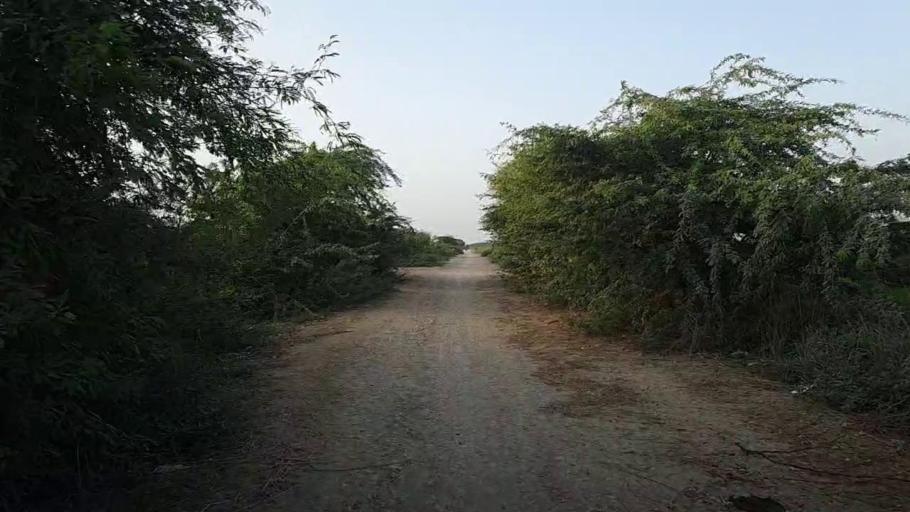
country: PK
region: Sindh
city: Kario
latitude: 24.7139
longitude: 68.4621
